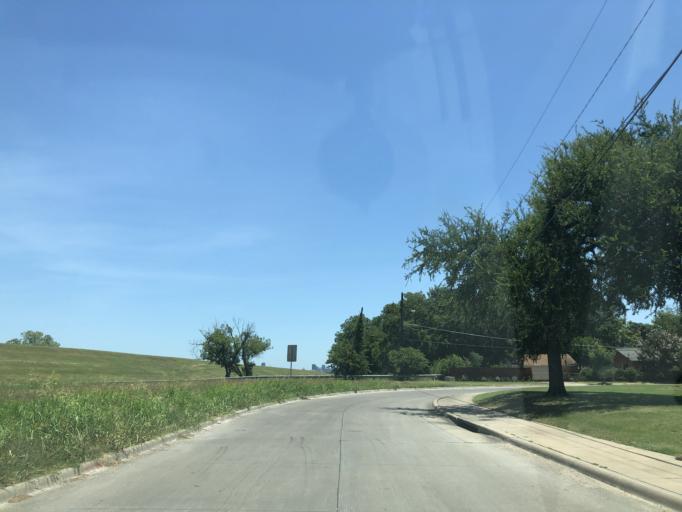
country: US
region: Texas
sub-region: Dallas County
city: Cockrell Hill
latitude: 32.7936
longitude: -96.8919
